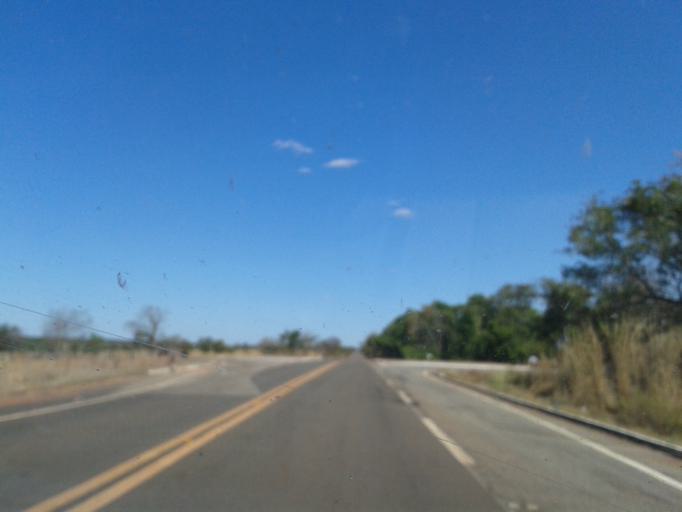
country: BR
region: Goias
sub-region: Sao Miguel Do Araguaia
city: Sao Miguel do Araguaia
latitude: -13.8898
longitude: -50.3287
